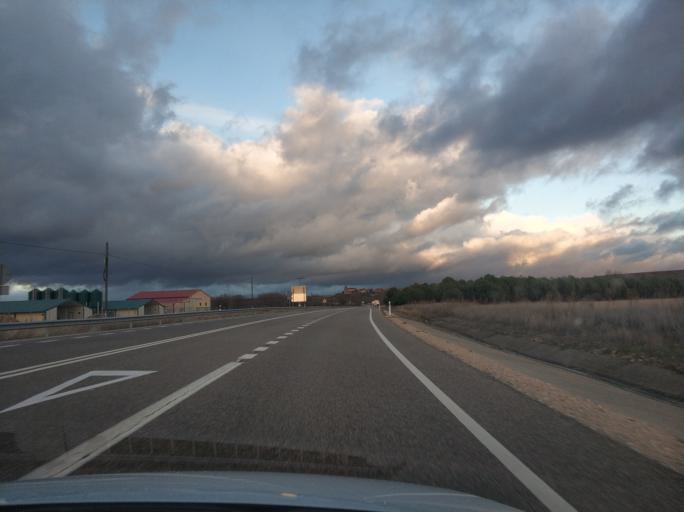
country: ES
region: Castille and Leon
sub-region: Provincia de Segovia
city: Ayllon
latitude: 41.4072
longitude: -3.4154
